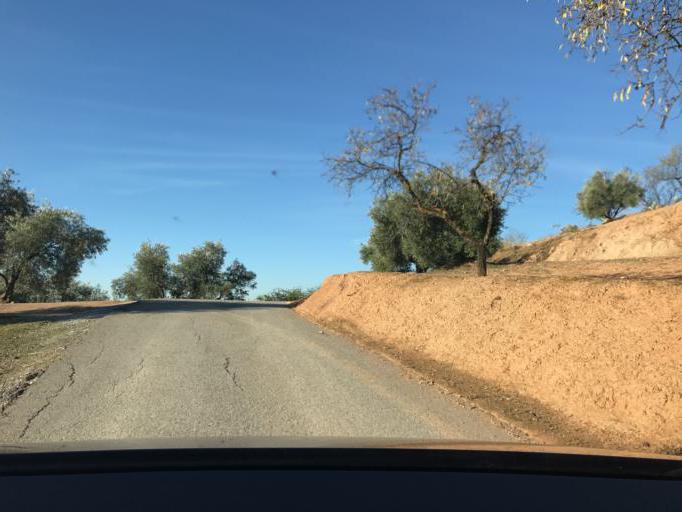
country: ES
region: Andalusia
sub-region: Provincia de Granada
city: Peligros
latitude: 37.2475
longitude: -3.6330
